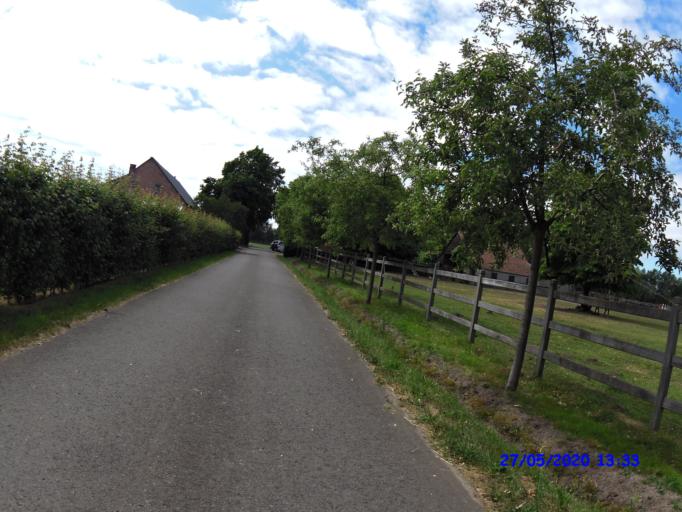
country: BE
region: Flanders
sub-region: Provincie Antwerpen
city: Kasterlee
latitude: 51.1996
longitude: 4.9559
